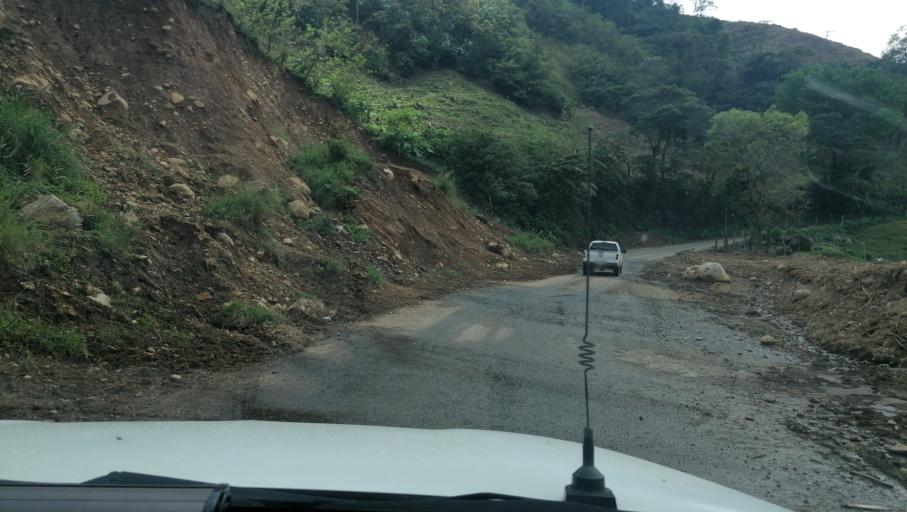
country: MX
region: Chiapas
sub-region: Francisco Leon
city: San Miguel la Sardina
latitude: 17.2479
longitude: -93.2845
